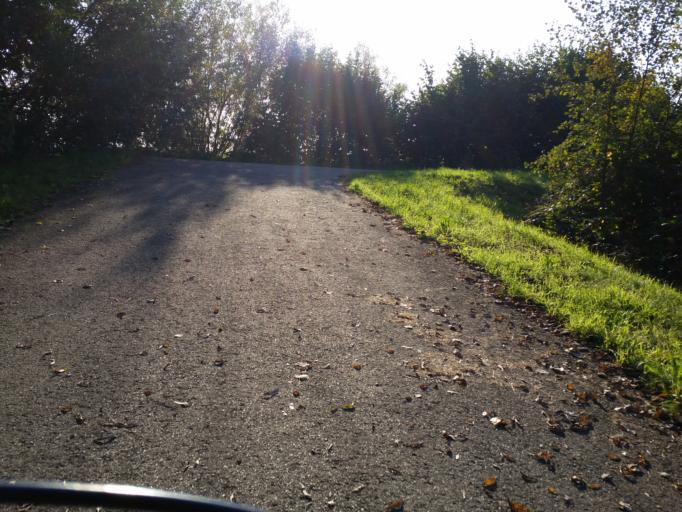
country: BE
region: Flanders
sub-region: Provincie Antwerpen
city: Niel
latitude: 51.0952
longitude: 4.3438
